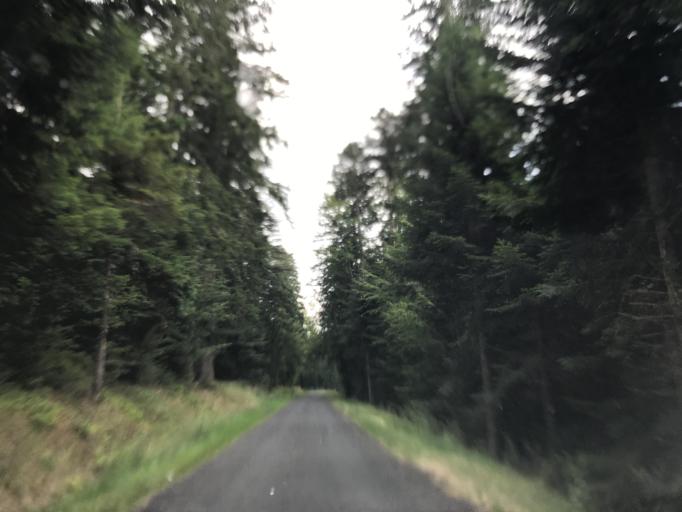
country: FR
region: Rhone-Alpes
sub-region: Departement de la Loire
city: Noiretable
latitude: 45.7642
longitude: 3.7279
